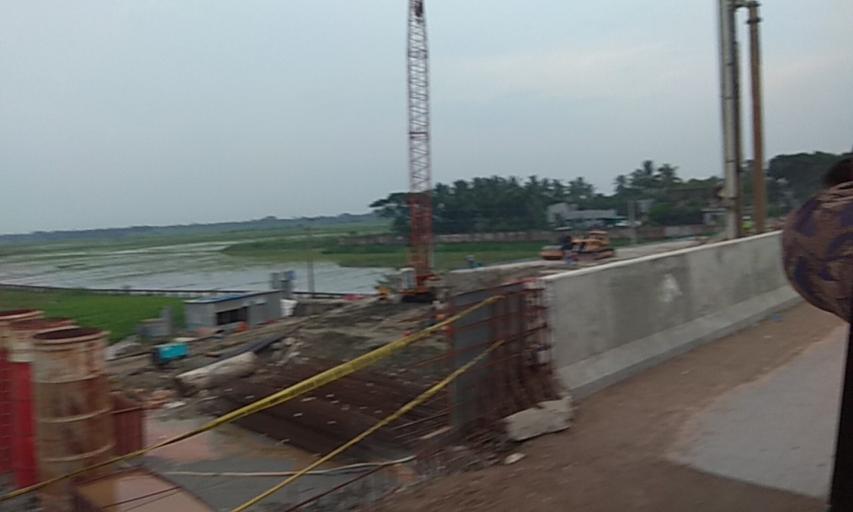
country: BD
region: Dhaka
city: Char Bhadrasan
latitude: 23.3885
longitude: 89.9876
